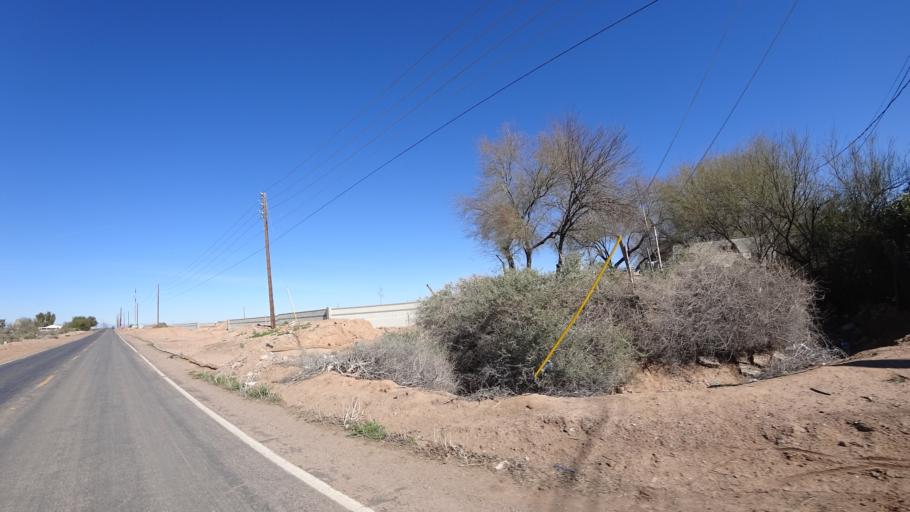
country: US
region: Arizona
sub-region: Maricopa County
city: Tolleson
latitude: 33.3952
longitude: -112.2891
